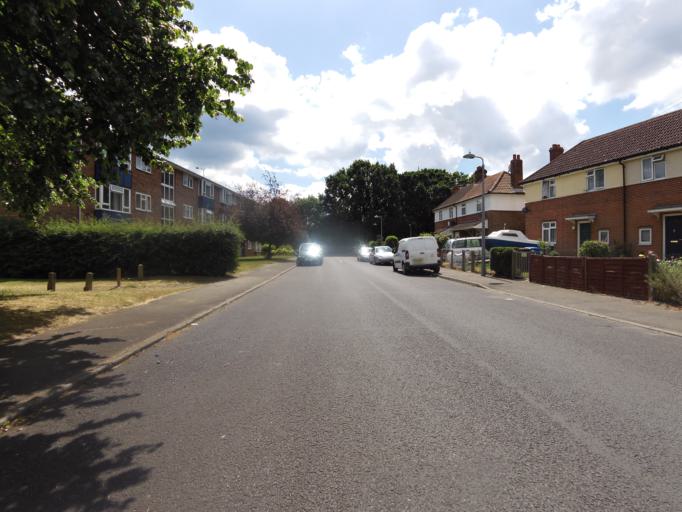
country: GB
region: England
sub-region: Suffolk
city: Ipswich
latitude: 52.0373
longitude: 1.1786
